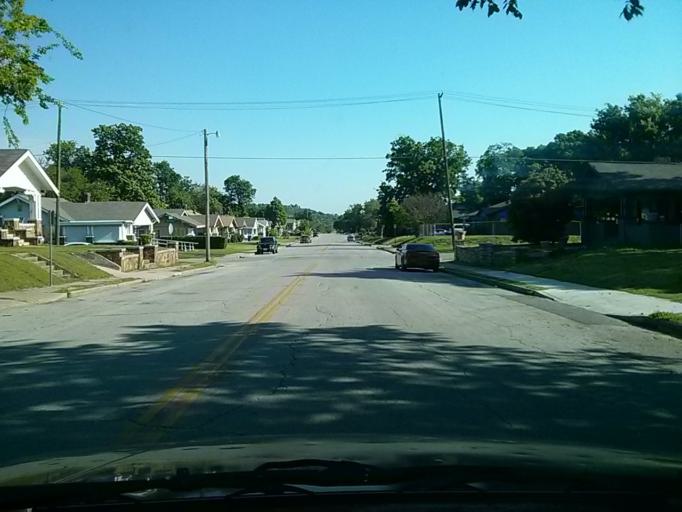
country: US
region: Oklahoma
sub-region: Tulsa County
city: Tulsa
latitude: 36.1710
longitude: -95.9968
